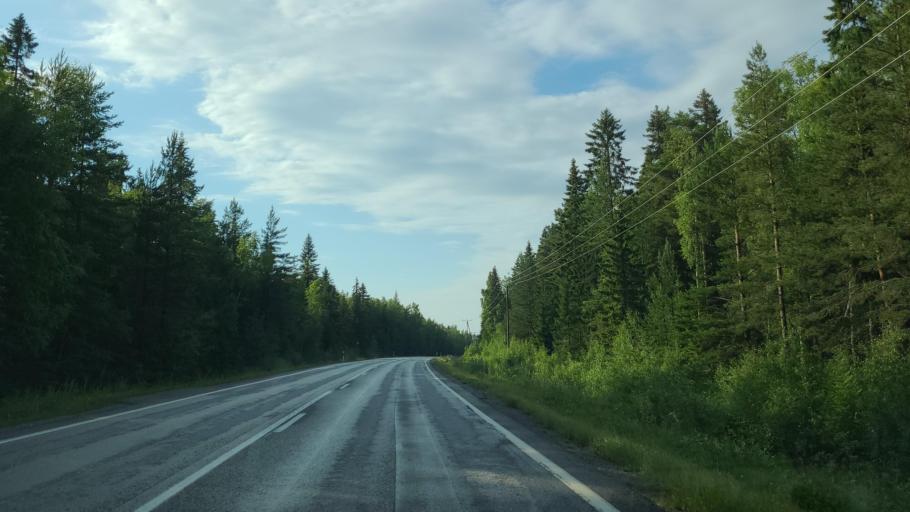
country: FI
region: Ostrobothnia
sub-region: Vaasa
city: Vaasa
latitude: 63.1830
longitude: 21.5694
